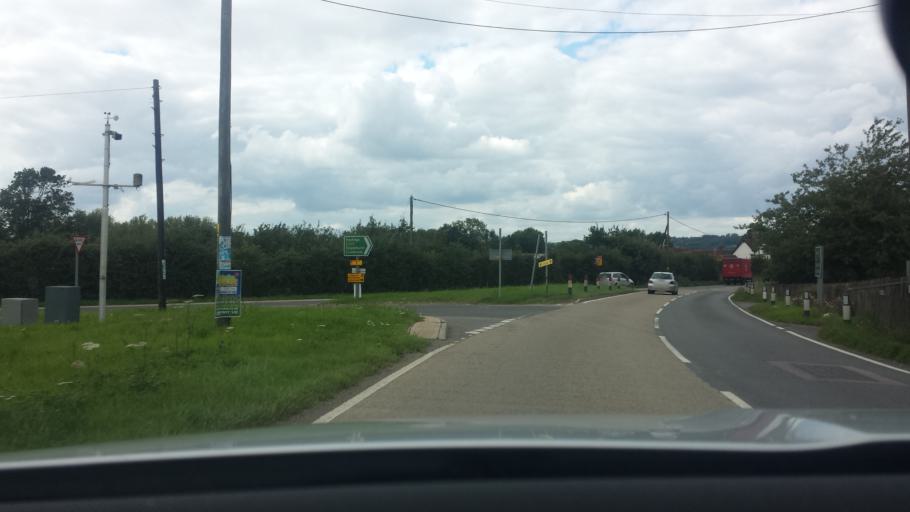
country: GB
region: England
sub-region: Kent
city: Marden
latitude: 51.1998
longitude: 0.5180
